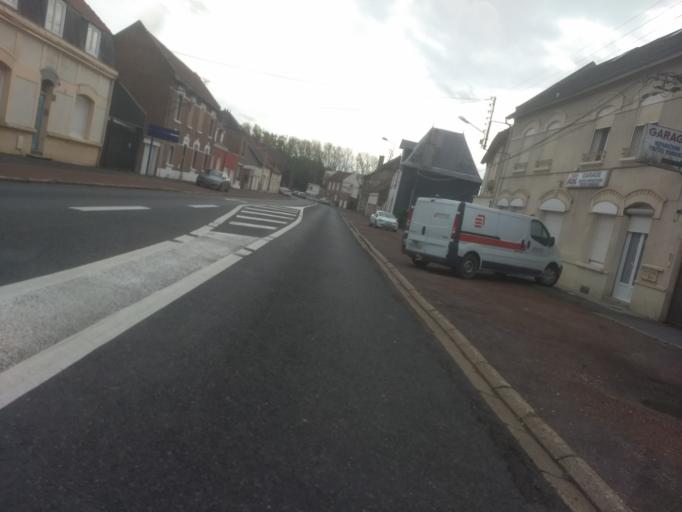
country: FR
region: Nord-Pas-de-Calais
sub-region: Departement du Pas-de-Calais
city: Beaurains
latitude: 50.2647
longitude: 2.7842
